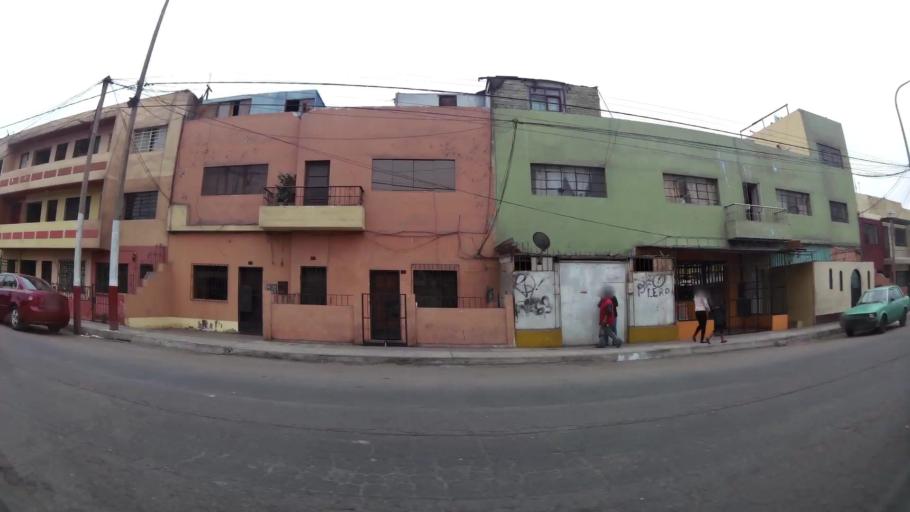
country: PE
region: Callao
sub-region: Callao
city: Callao
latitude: -12.0544
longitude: -77.1336
